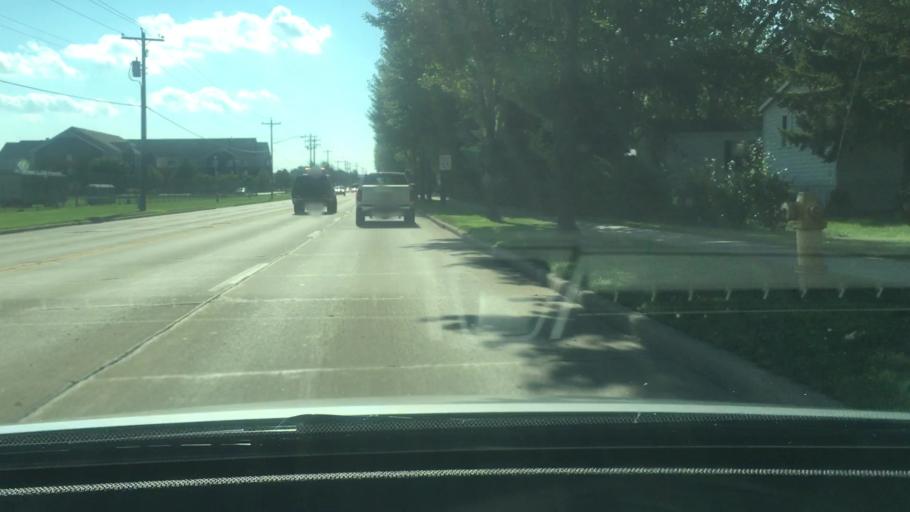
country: US
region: Wisconsin
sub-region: Winnebago County
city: Oshkosh
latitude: 43.9961
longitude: -88.5682
